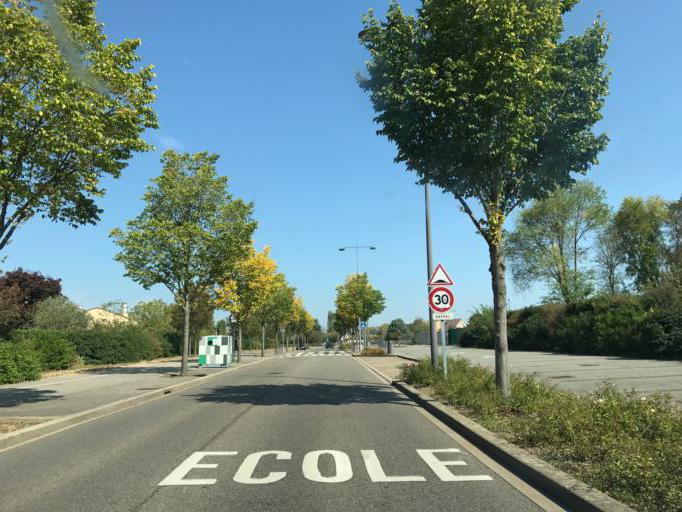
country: FR
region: Rhone-Alpes
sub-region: Departement du Rhone
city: Meyzieu
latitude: 45.7708
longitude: 4.9932
